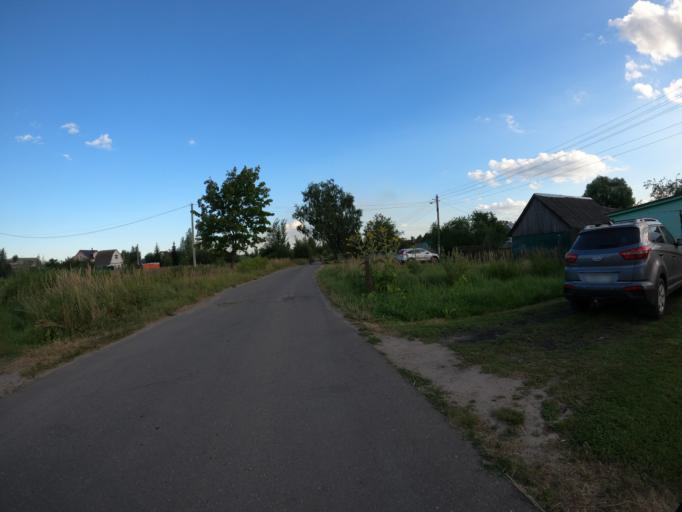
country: RU
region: Moskovskaya
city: Ashitkovo
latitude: 55.4251
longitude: 38.5815
